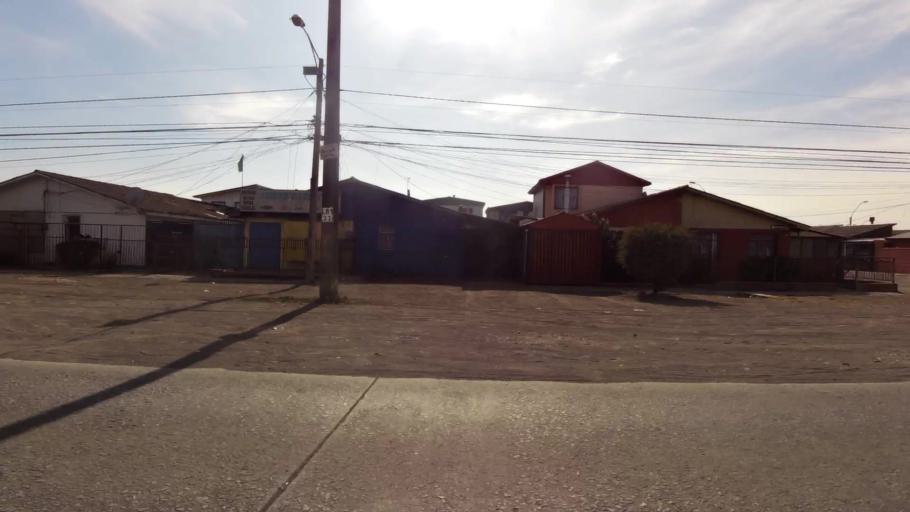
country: CL
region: Biobio
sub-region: Provincia de Concepcion
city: Talcahuano
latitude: -36.7843
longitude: -73.1108
